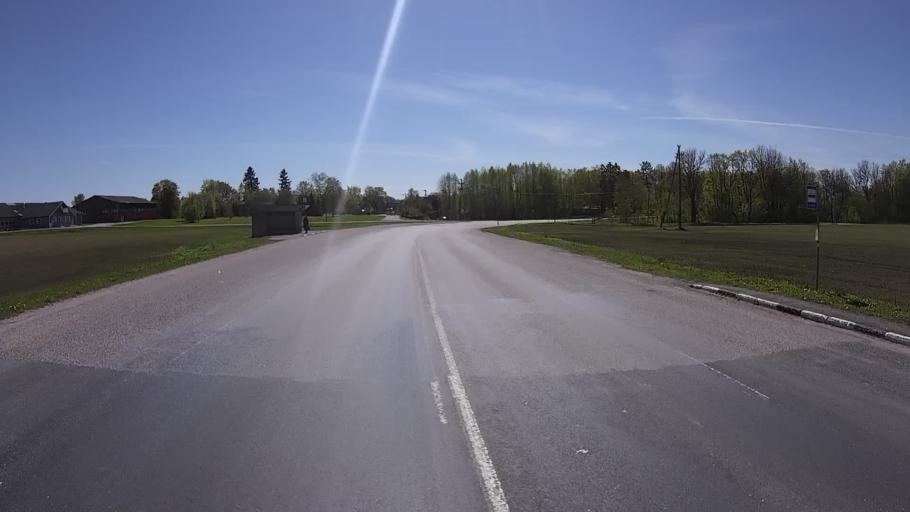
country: EE
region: Harju
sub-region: Anija vald
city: Kehra
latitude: 59.1293
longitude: 25.2045
